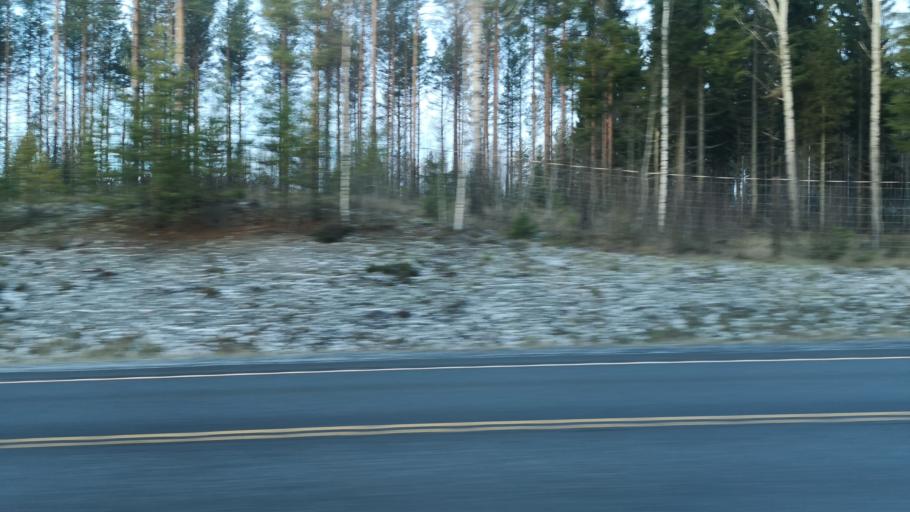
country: FI
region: Southern Savonia
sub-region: Mikkeli
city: Pertunmaa
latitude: 61.3719
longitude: 26.2919
